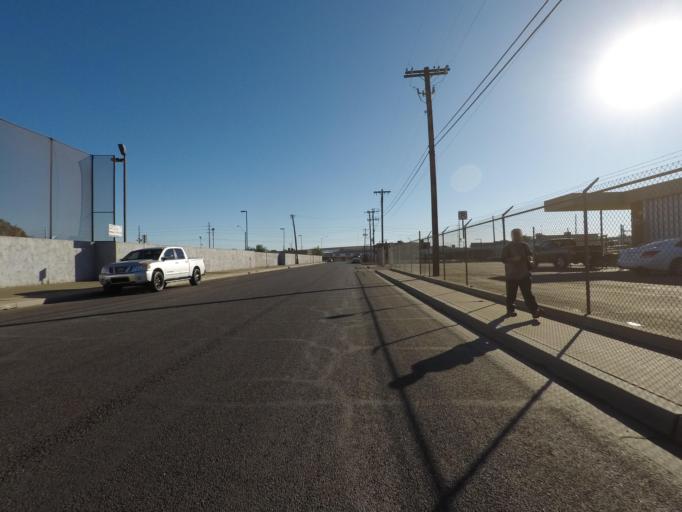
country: US
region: Arizona
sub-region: Maricopa County
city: Phoenix
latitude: 33.4674
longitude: -112.1064
